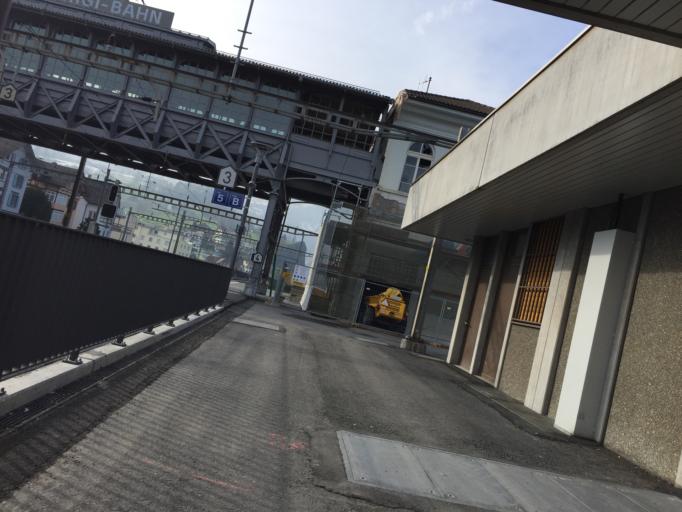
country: CH
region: Schwyz
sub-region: Bezirk Schwyz
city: Goldau
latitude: 47.0491
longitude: 8.5483
